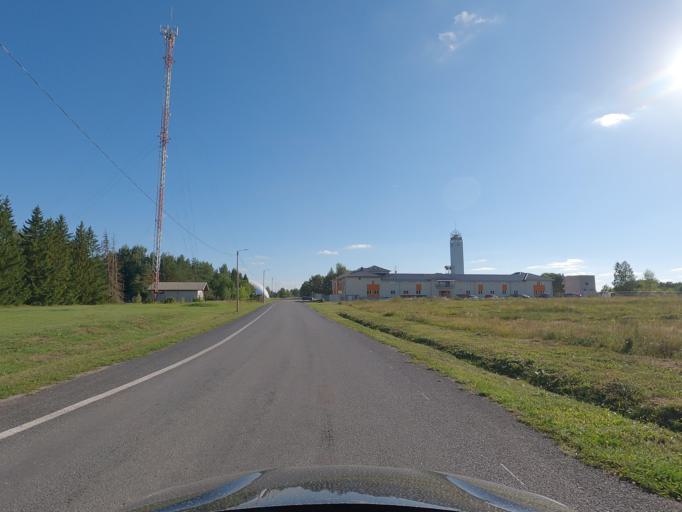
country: EE
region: Raplamaa
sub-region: Rapla vald
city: Rapla
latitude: 59.0071
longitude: 24.7849
